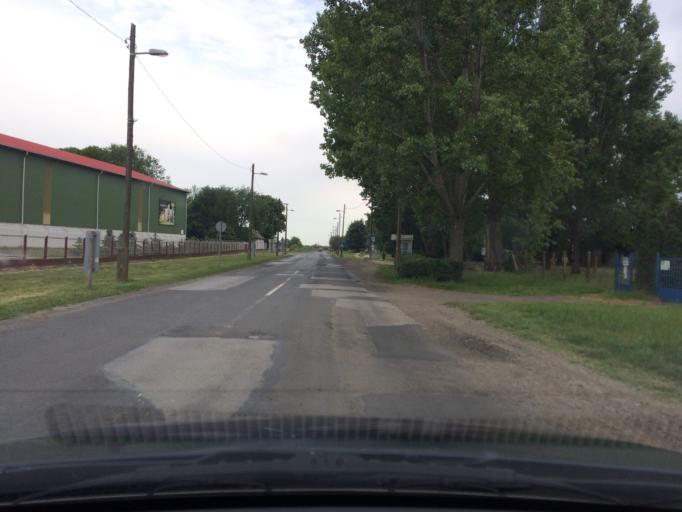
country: HU
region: Hajdu-Bihar
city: Hajdunanas
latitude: 47.9050
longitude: 21.4044
